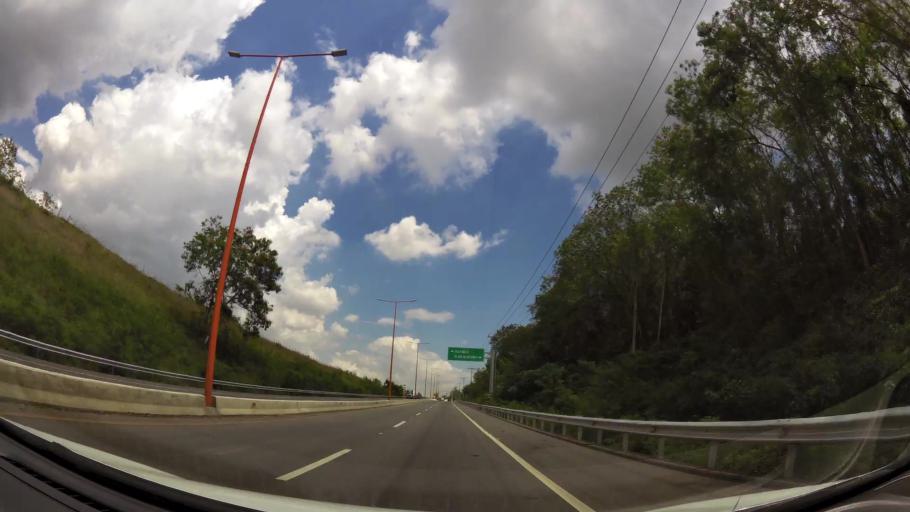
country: DO
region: Nacional
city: La Agustina
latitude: 18.5416
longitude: -69.9581
